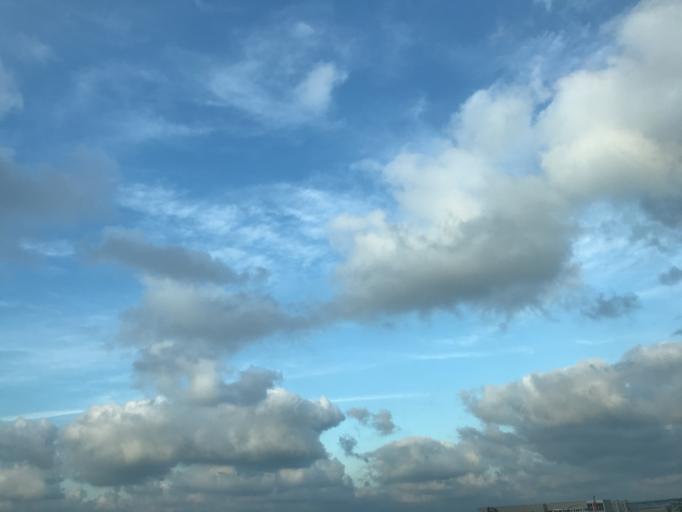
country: TR
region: Istanbul
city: Durusu
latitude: 41.2550
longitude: 28.7096
